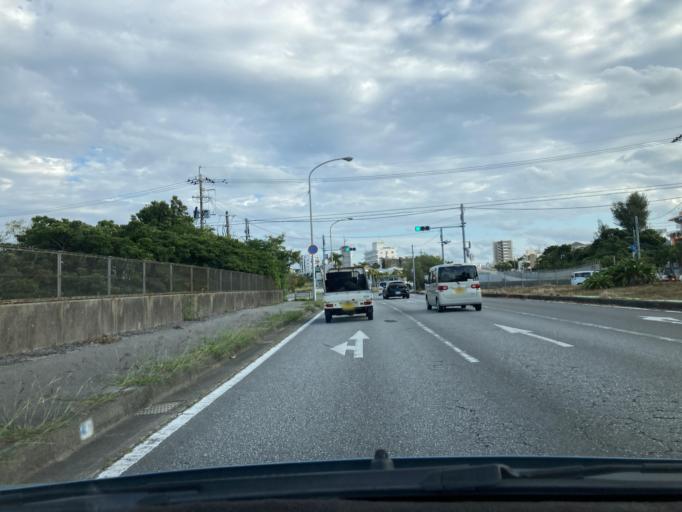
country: JP
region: Okinawa
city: Okinawa
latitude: 26.3307
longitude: 127.7842
